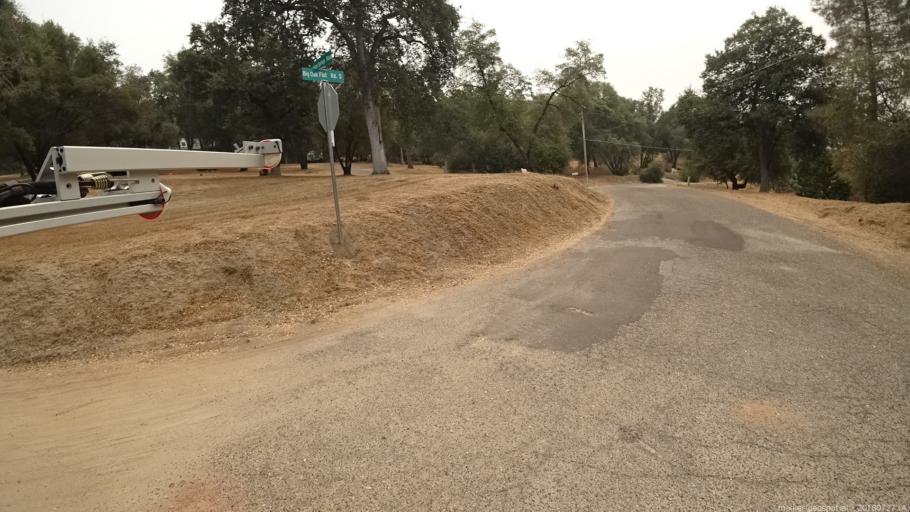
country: US
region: California
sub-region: Madera County
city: Oakhurst
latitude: 37.3383
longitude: -119.6323
